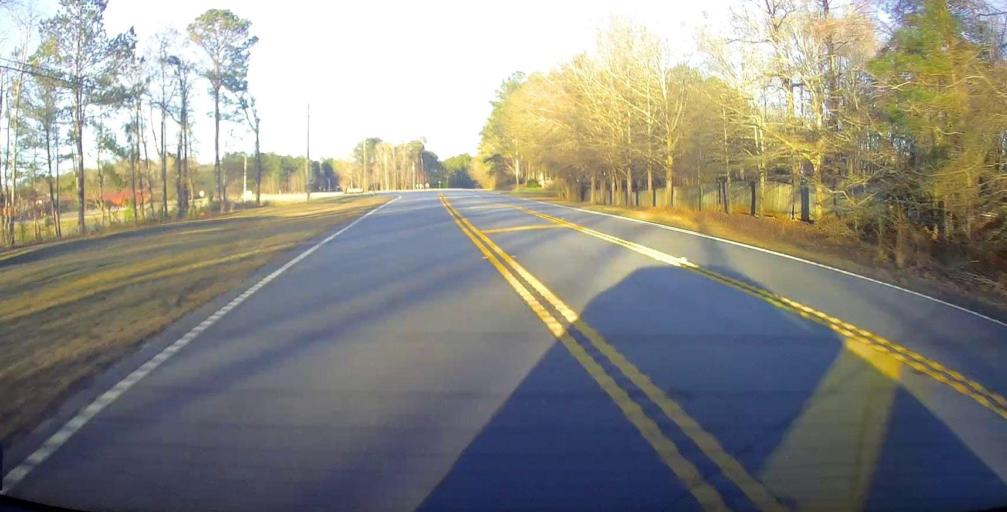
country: US
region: Georgia
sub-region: Harris County
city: Hamilton
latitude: 32.6735
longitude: -84.9195
